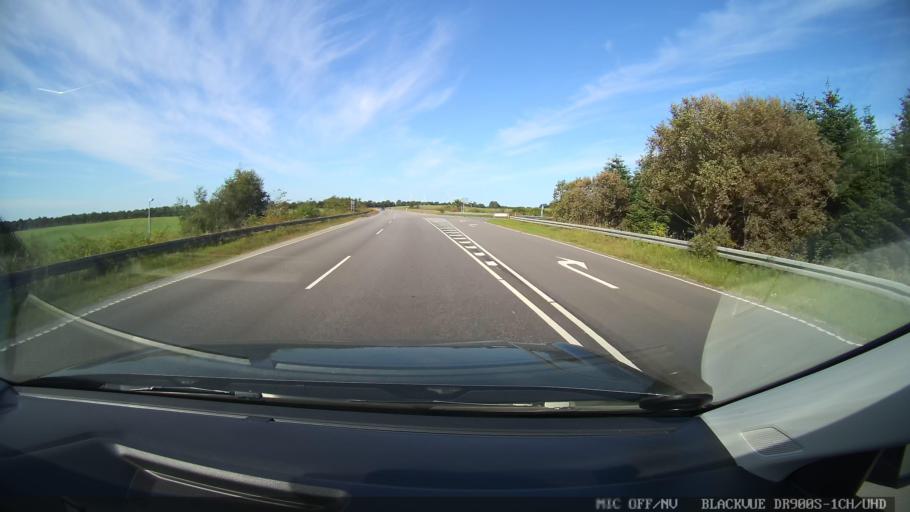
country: DK
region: North Denmark
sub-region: Mariagerfjord Kommune
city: Hobro
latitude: 56.6665
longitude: 9.7665
